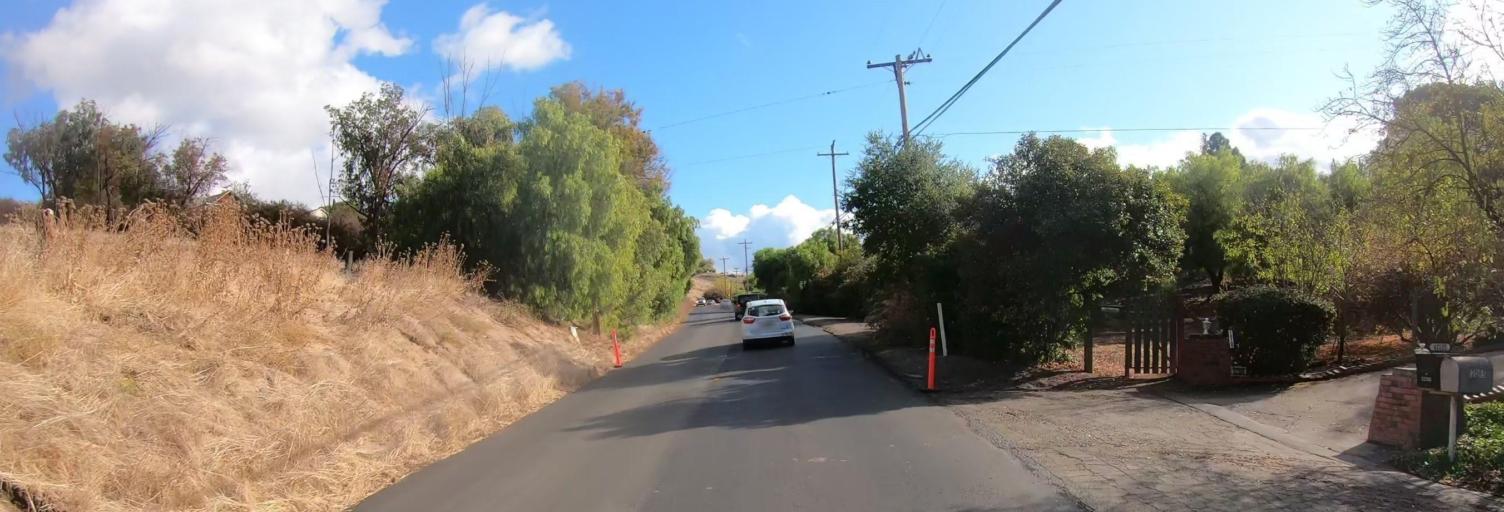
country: US
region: California
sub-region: Santa Clara County
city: East Foothills
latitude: 37.3761
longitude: -121.8006
